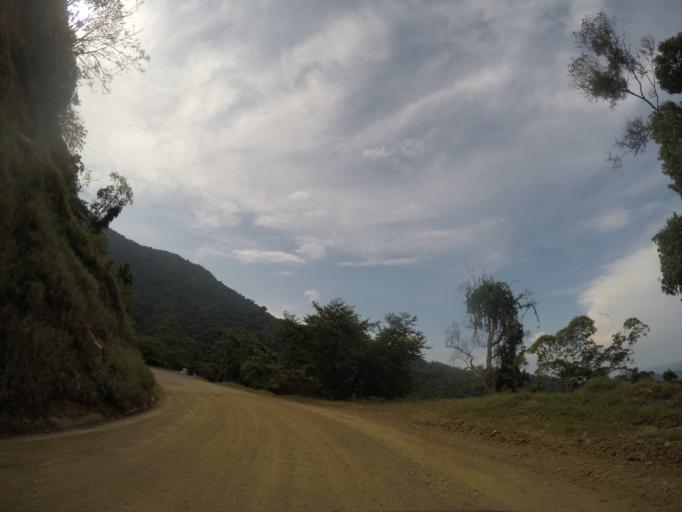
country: MX
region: Oaxaca
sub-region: San Pedro Pochutla
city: Los Naranjos Esquipulas
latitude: 15.9507
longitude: -96.4451
